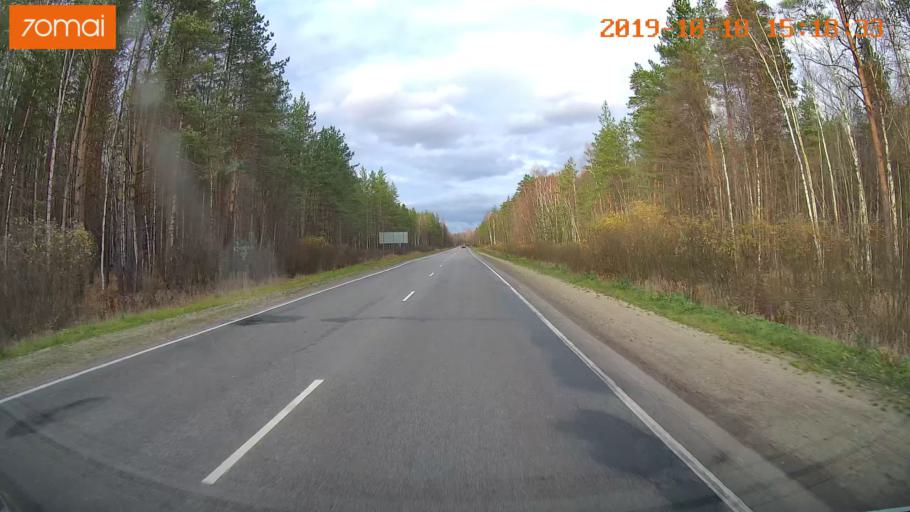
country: RU
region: Vladimir
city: Anopino
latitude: 55.6609
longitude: 40.7299
